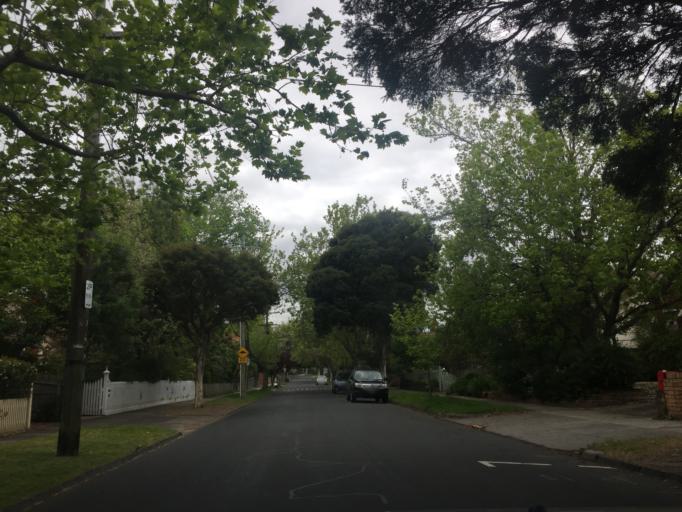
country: AU
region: Victoria
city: Balwyn
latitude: -37.8208
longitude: 145.0618
